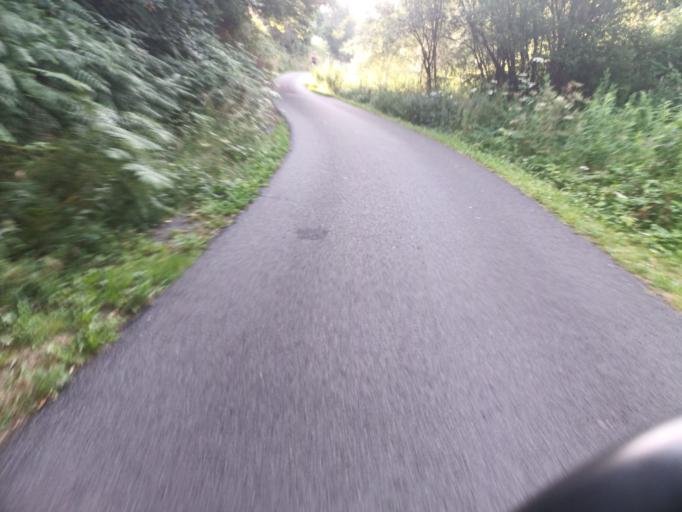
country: GB
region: Northern Ireland
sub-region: Castlereagh District
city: Dundonald
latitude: 54.5884
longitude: -5.8069
